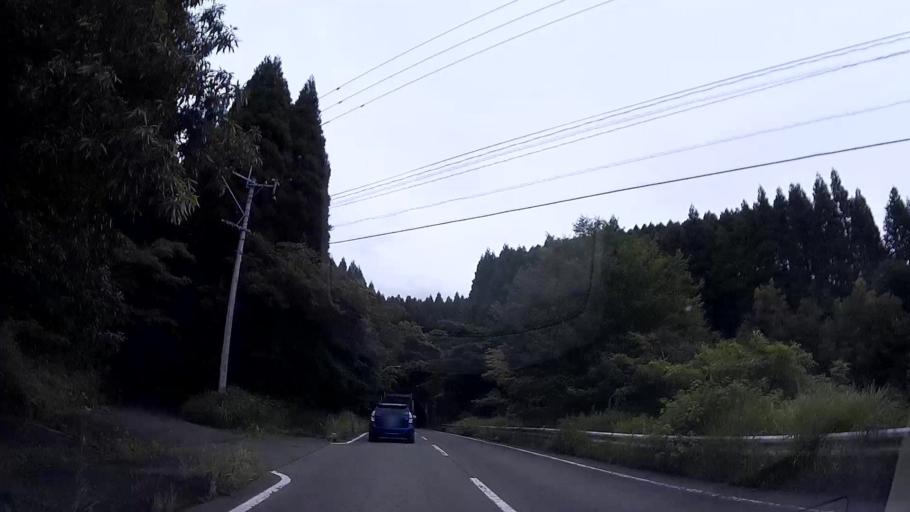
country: JP
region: Kumamoto
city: Aso
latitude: 33.1219
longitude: 131.0137
